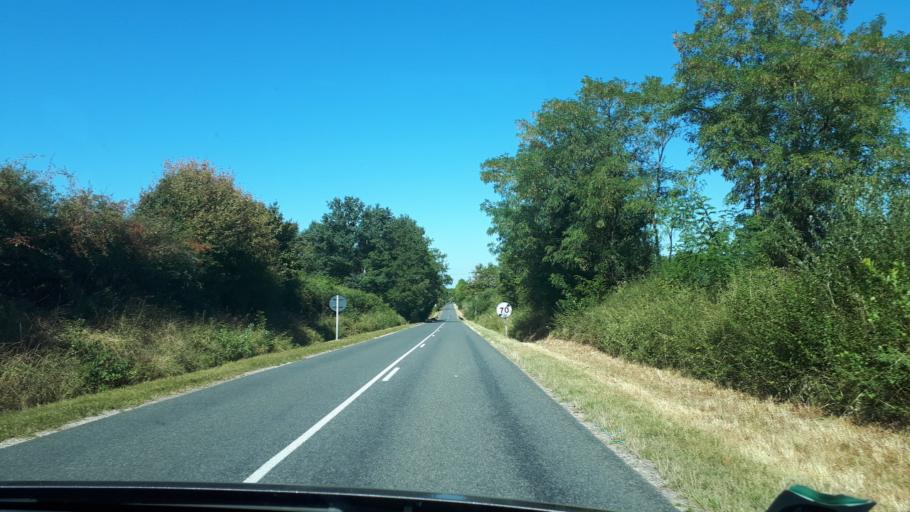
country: FR
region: Centre
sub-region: Departement du Loiret
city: Coullons
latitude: 47.6205
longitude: 2.5117
